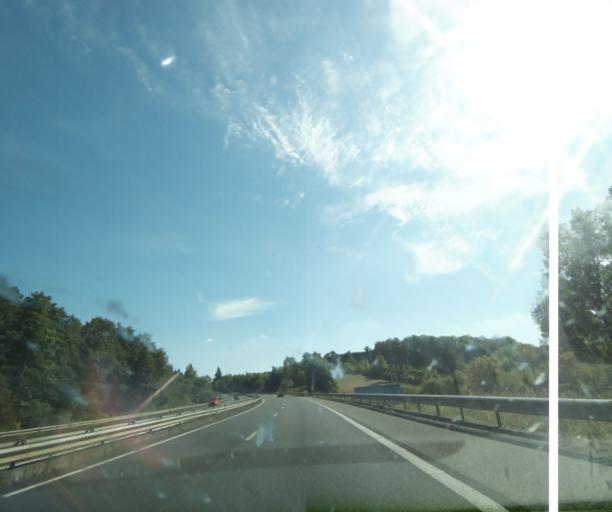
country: FR
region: Limousin
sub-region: Departement de la Correze
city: Brive-la-Gaillarde
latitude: 45.1288
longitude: 1.4922
